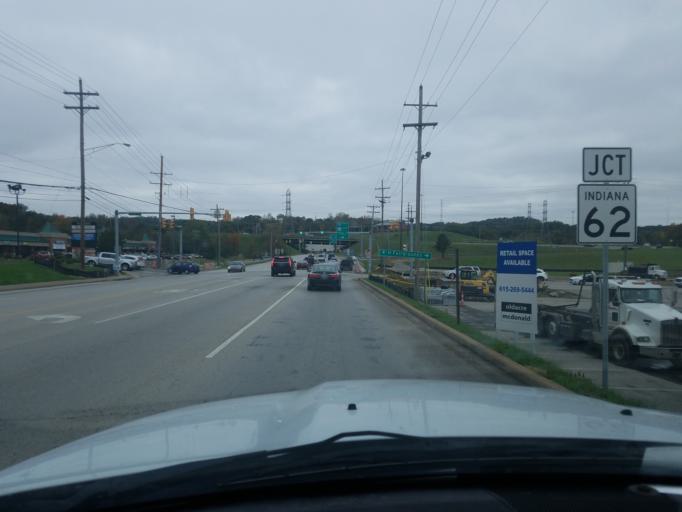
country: US
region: Indiana
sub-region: Floyd County
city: New Albany
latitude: 38.3086
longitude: -85.8434
